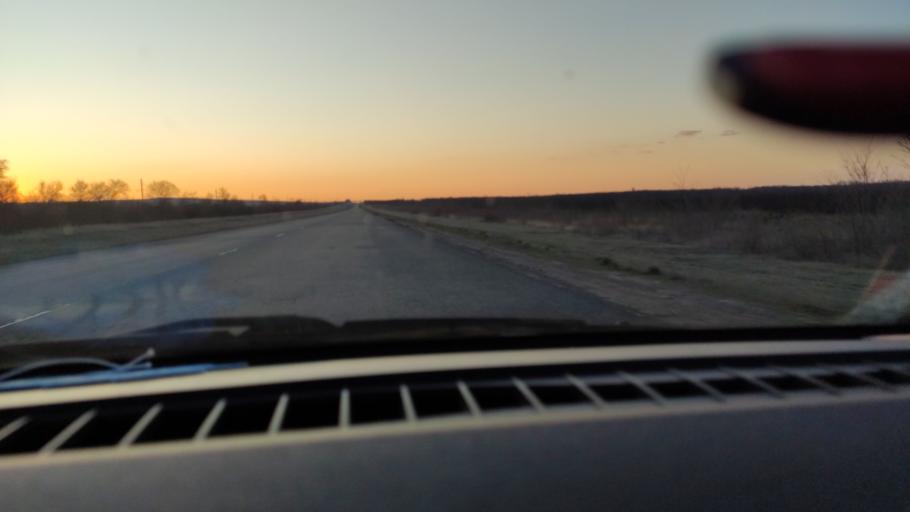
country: RU
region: Saratov
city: Yelshanka
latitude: 51.8294
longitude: 46.2483
